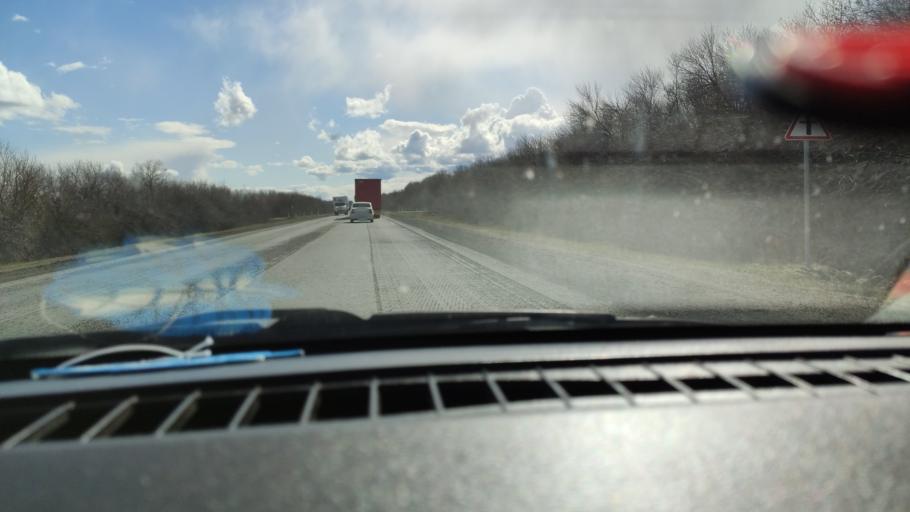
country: RU
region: Saratov
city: Dukhovnitskoye
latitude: 52.6448
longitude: 48.1949
